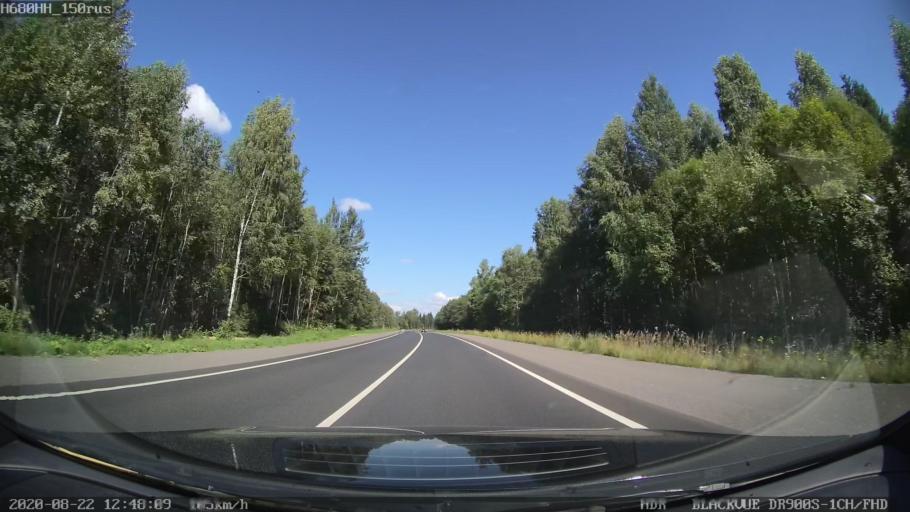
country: RU
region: Tverskaya
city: Rameshki
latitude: 57.4358
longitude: 36.1818
